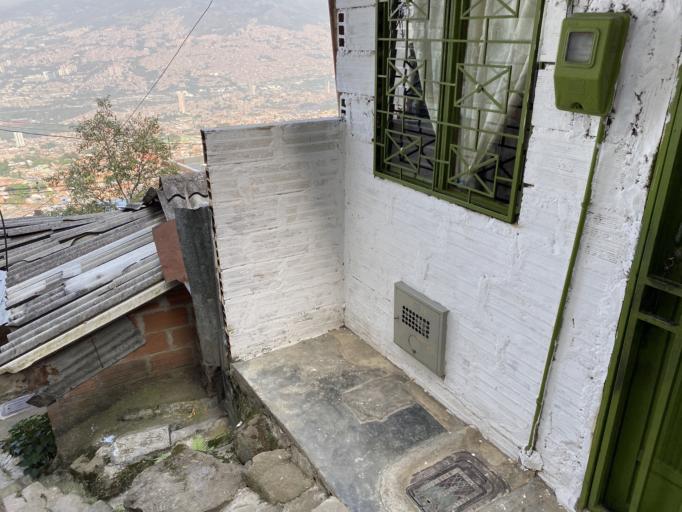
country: CO
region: Antioquia
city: Medellin
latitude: 6.2642
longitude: -75.5422
